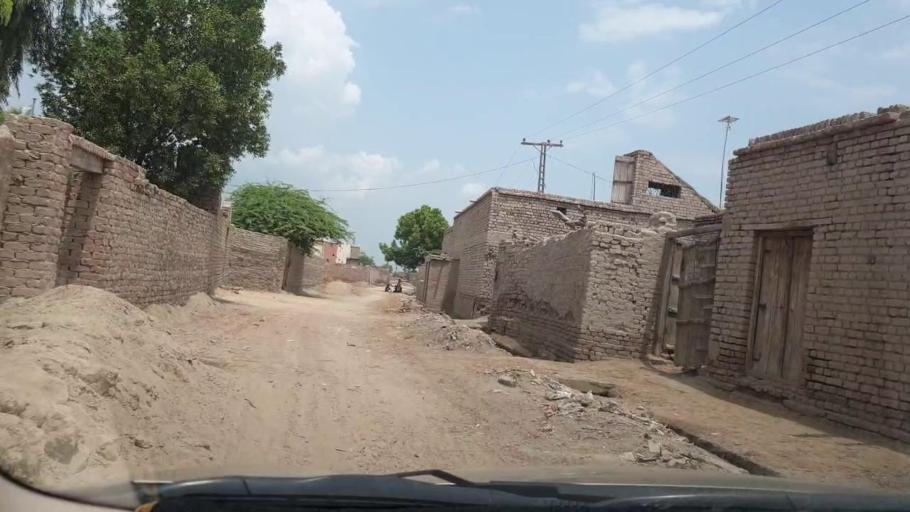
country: PK
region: Sindh
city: Larkana
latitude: 27.5653
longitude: 68.1258
